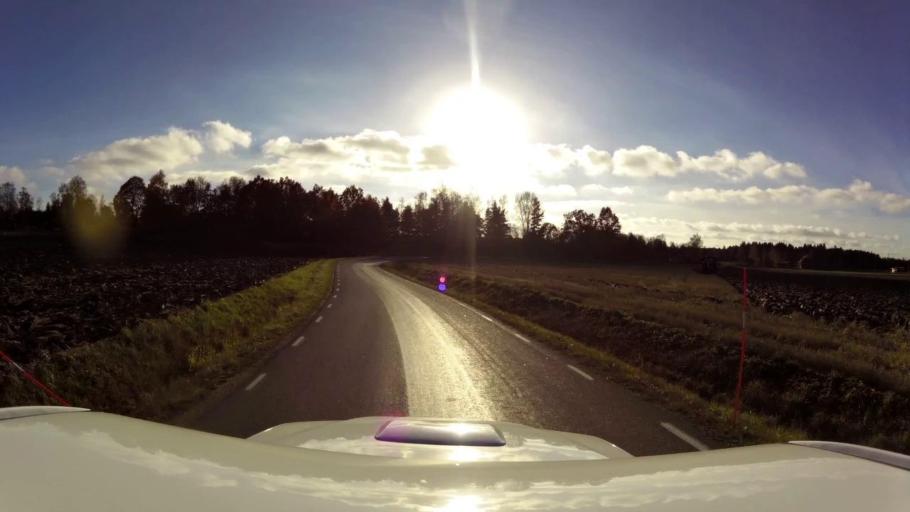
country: SE
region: OEstergoetland
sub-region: Linkopings Kommun
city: Vikingstad
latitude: 58.2851
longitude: 15.4399
